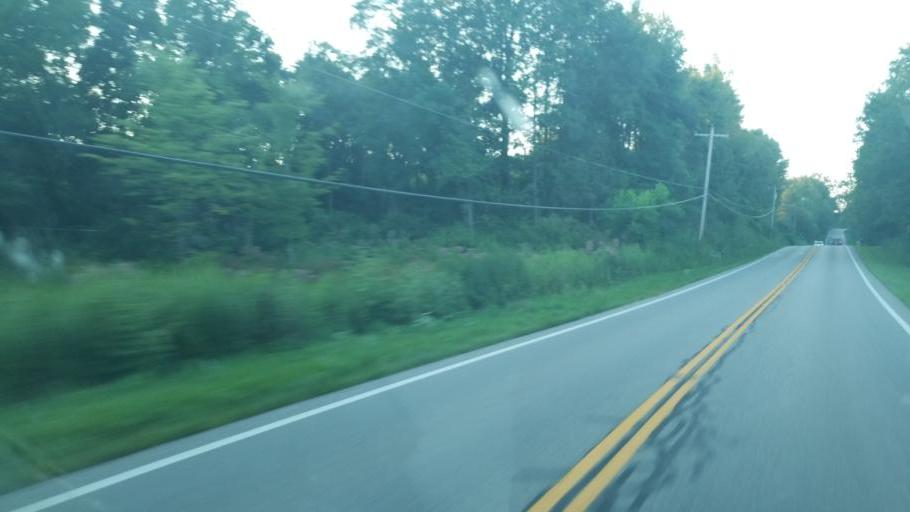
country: US
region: Ohio
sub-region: Trumbull County
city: Newton Falls
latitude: 41.2095
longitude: -80.9787
